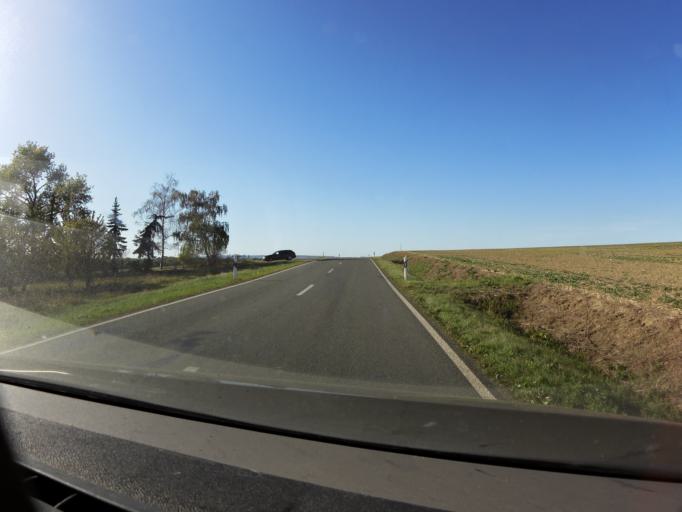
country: DE
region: Saxony-Anhalt
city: Hedersleben
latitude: 51.8693
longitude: 11.2431
